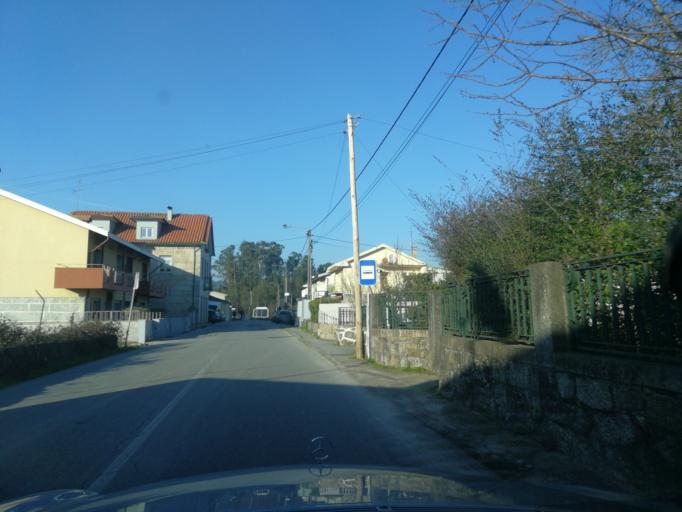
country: PT
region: Braga
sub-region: Guimaraes
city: Ponte
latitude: 41.4900
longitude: -8.3394
